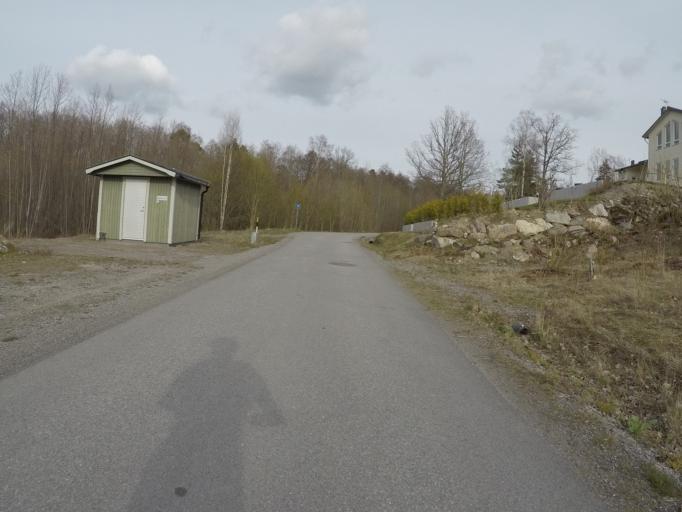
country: SE
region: Soedermanland
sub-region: Eskilstuna Kommun
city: Torshalla
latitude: 59.4463
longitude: 16.5259
